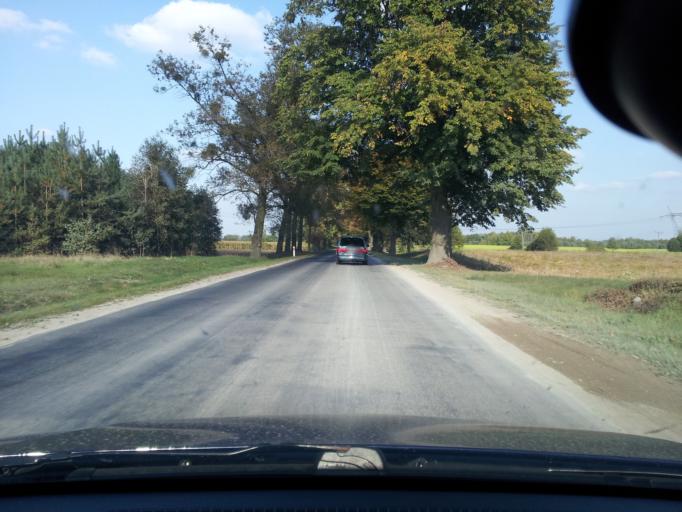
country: PL
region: Kujawsko-Pomorskie
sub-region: Powiat lipnowski
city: Chrostkowo
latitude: 52.9612
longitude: 19.3127
